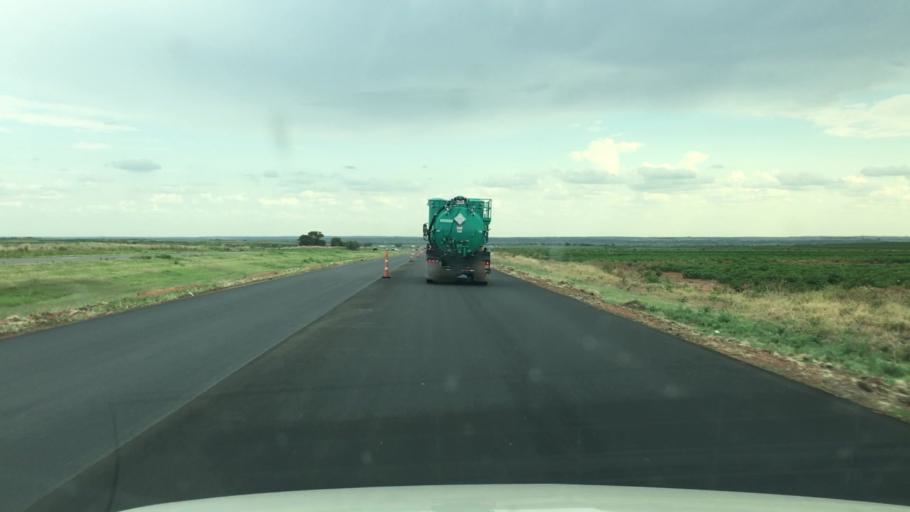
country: US
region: Texas
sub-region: Hall County
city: Memphis
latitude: 34.6129
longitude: -100.4696
